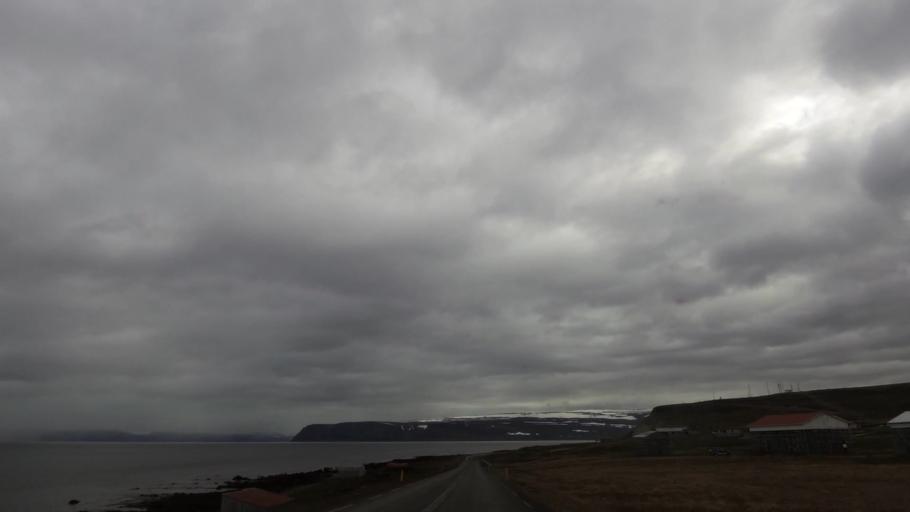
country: IS
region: Westfjords
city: Isafjoerdur
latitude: 66.0941
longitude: -23.0545
